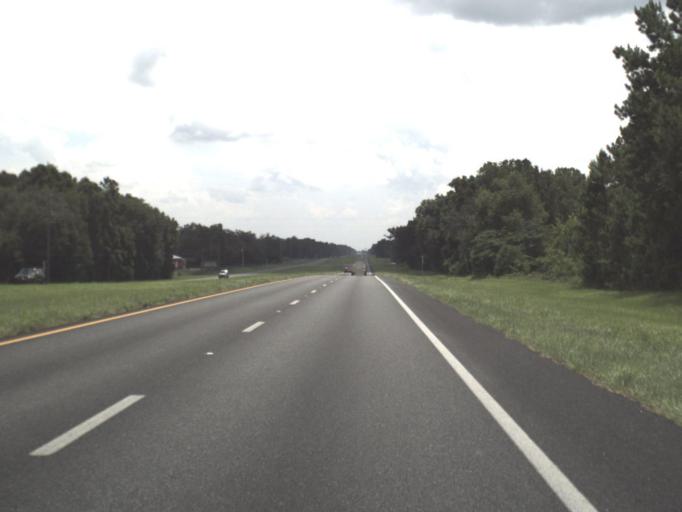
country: US
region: Florida
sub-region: Levy County
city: Williston
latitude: 29.4022
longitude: -82.5116
